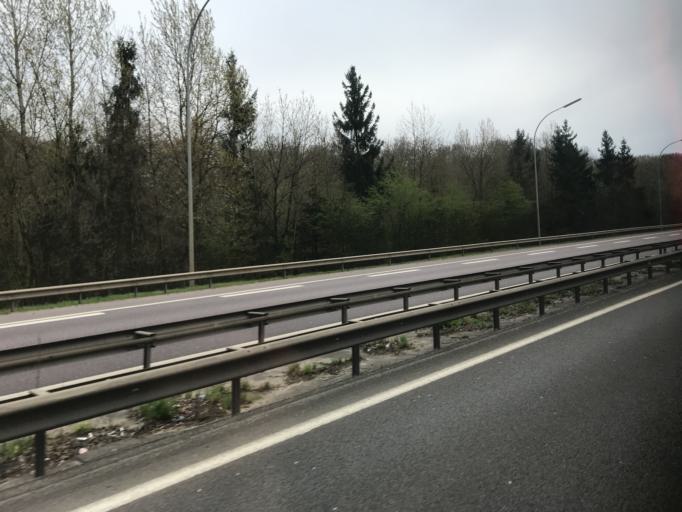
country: LU
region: Luxembourg
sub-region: Canton d'Esch-sur-Alzette
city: Leudelange
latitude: 49.5734
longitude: 6.0884
